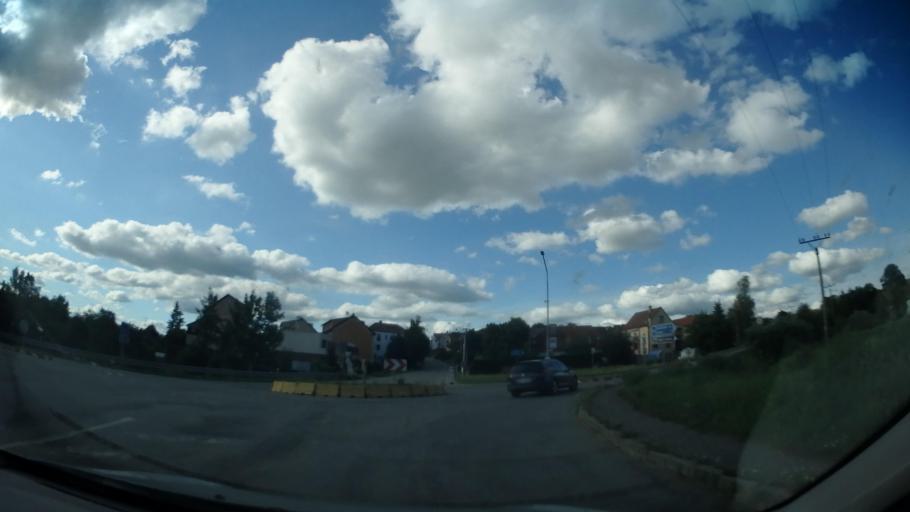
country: CZ
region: South Moravian
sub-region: Okres Blansko
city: Rajec-Jestrebi
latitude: 49.4041
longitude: 16.6419
